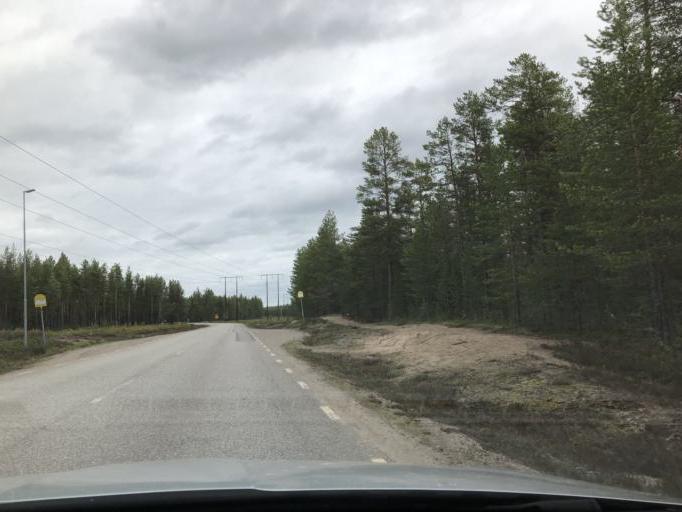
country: SE
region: Norrbotten
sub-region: Pitea Kommun
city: Pitea
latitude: 65.2390
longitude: 21.5208
